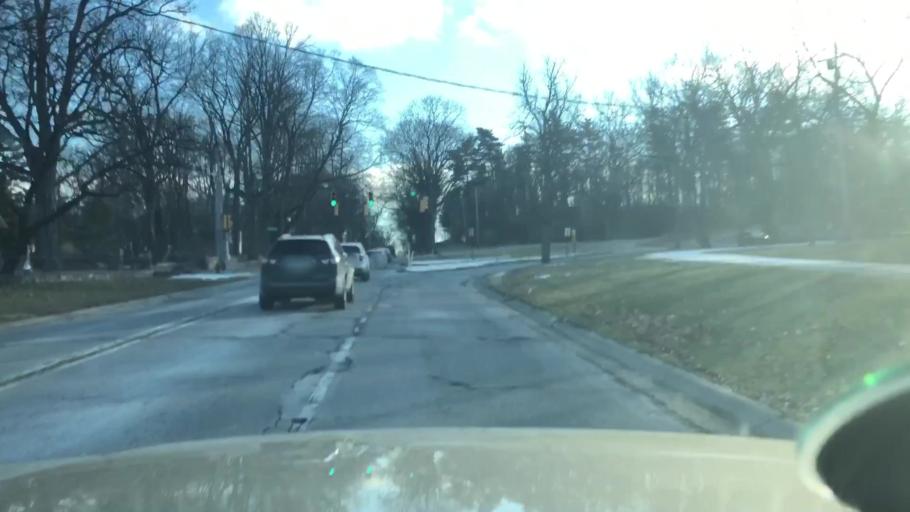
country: US
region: Michigan
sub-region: Jackson County
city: Vandercook Lake
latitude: 42.2153
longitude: -84.4183
